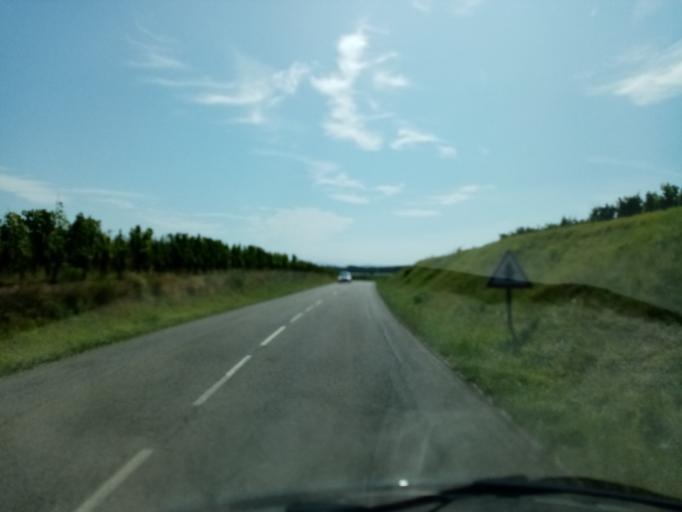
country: FR
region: Alsace
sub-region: Departement du Haut-Rhin
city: Bennwihr
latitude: 48.1415
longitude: 7.3332
